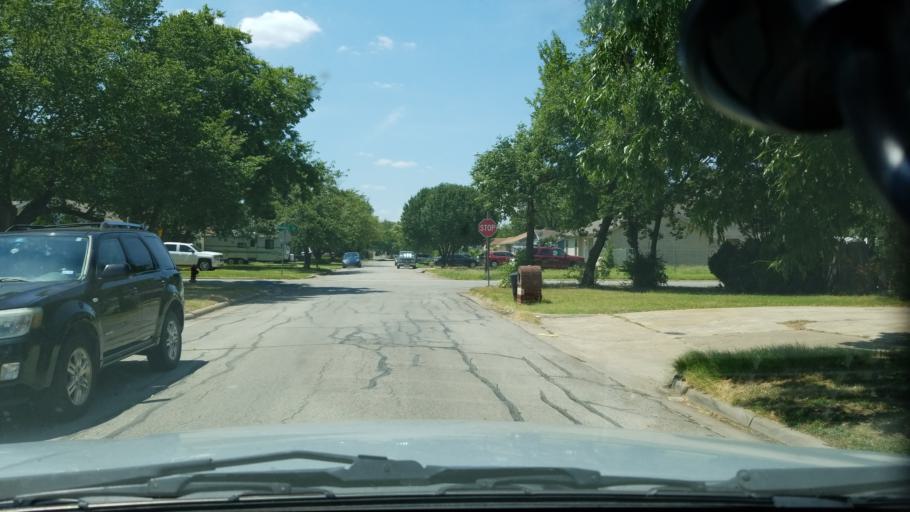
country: US
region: Texas
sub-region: Dallas County
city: Grand Prairie
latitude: 32.7520
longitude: -96.9538
